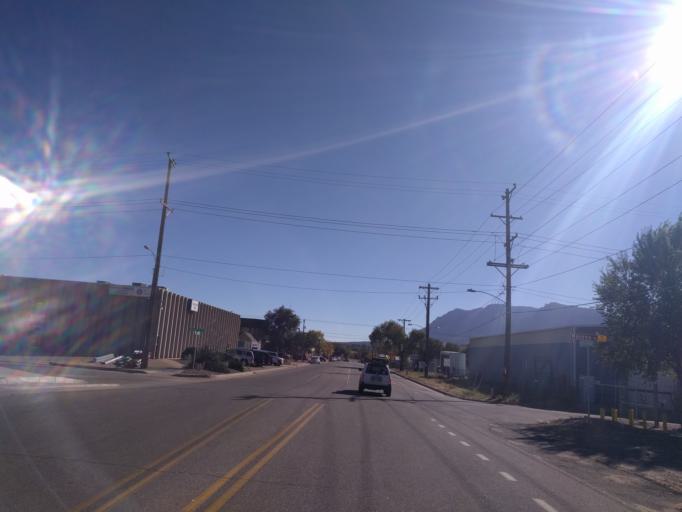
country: US
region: Colorado
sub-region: El Paso County
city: Colorado Springs
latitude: 38.8259
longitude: -104.8294
